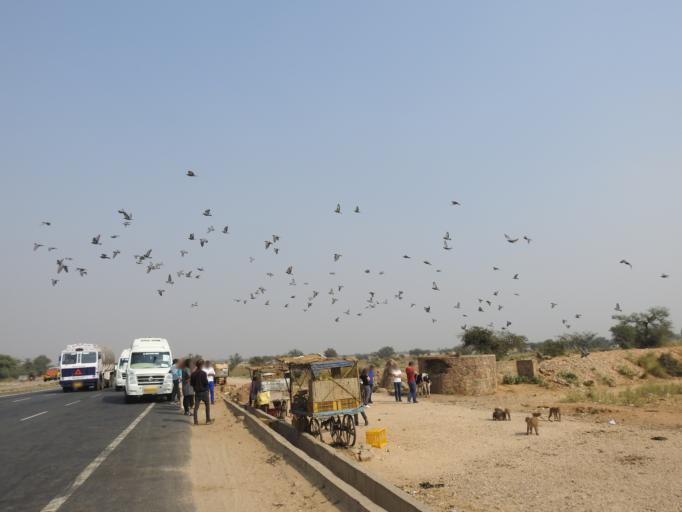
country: IN
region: Rajasthan
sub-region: Jaipur
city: Shahpura
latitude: 27.4169
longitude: 76.0008
